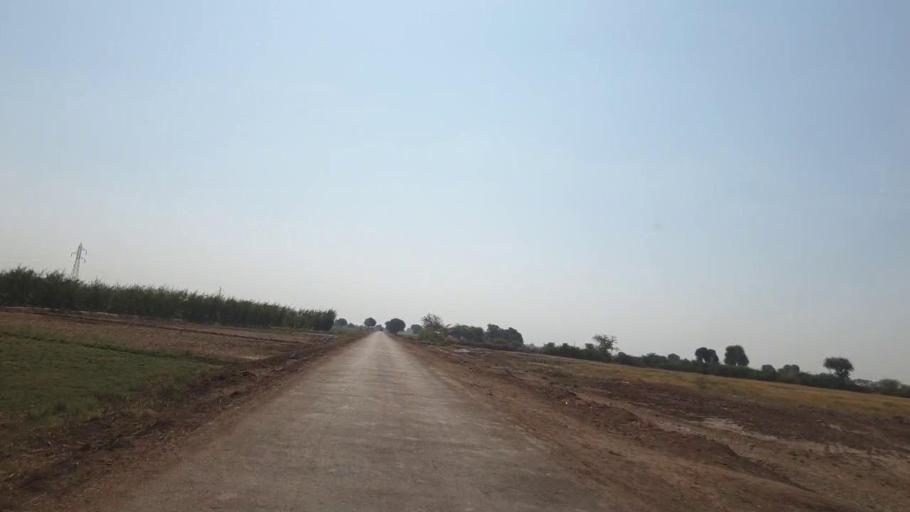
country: PK
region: Sindh
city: Kunri
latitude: 25.1676
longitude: 69.5457
